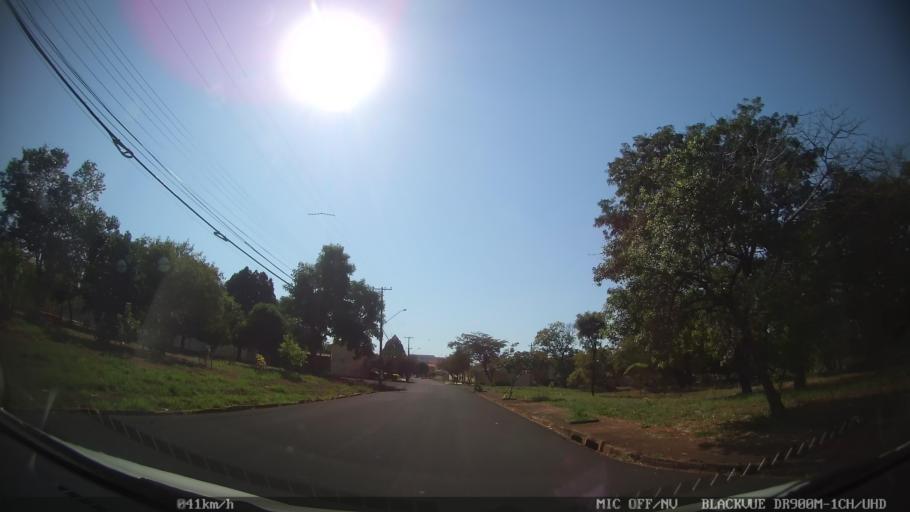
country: BR
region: Sao Paulo
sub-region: Ribeirao Preto
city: Ribeirao Preto
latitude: -21.2079
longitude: -47.7739
